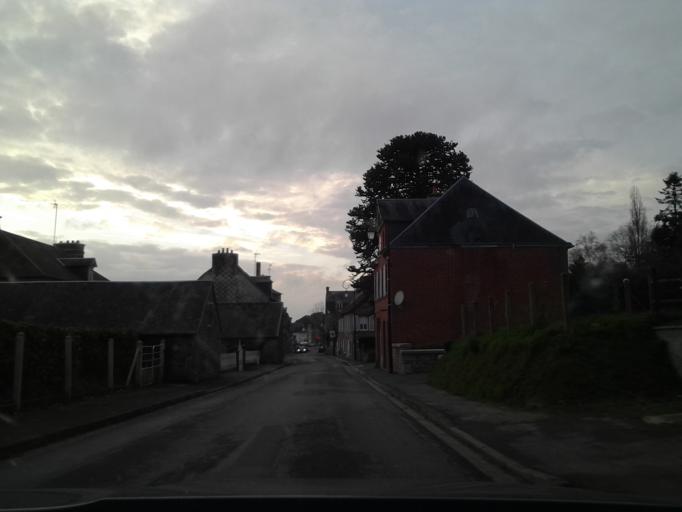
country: FR
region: Lower Normandy
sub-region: Departement du Calvados
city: Saint-Martin-des-Besaces
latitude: 48.9367
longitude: -0.8366
